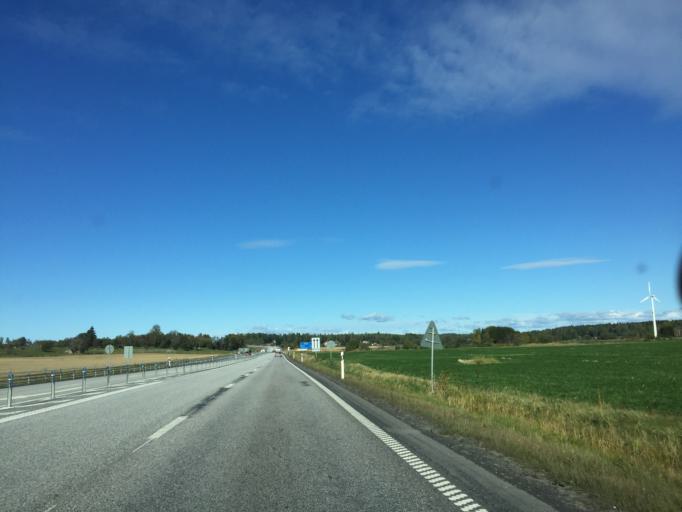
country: SE
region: OErebro
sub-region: Orebro Kommun
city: Hovsta
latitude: 59.3548
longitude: 15.2350
